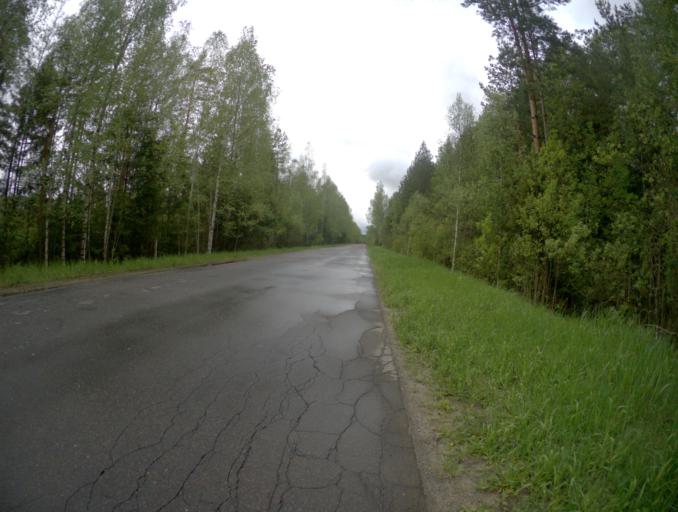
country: RU
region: Vladimir
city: Zolotkovo
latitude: 55.3466
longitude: 40.9712
